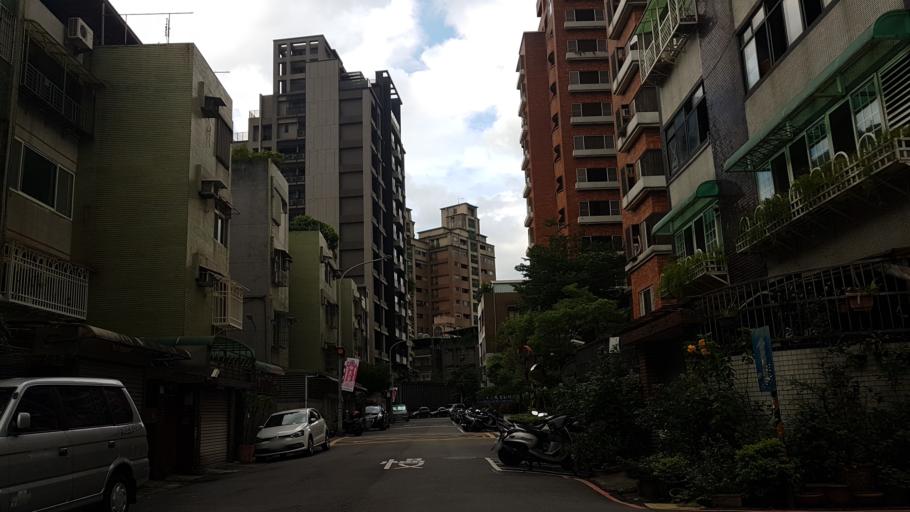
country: TW
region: Taipei
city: Taipei
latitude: 24.9901
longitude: 121.5665
